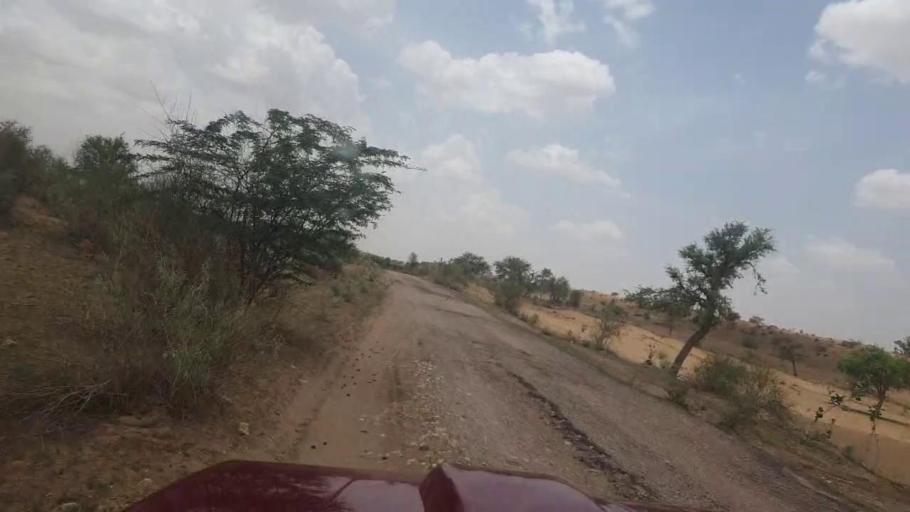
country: PK
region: Sindh
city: Islamkot
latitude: 25.2144
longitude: 70.4583
